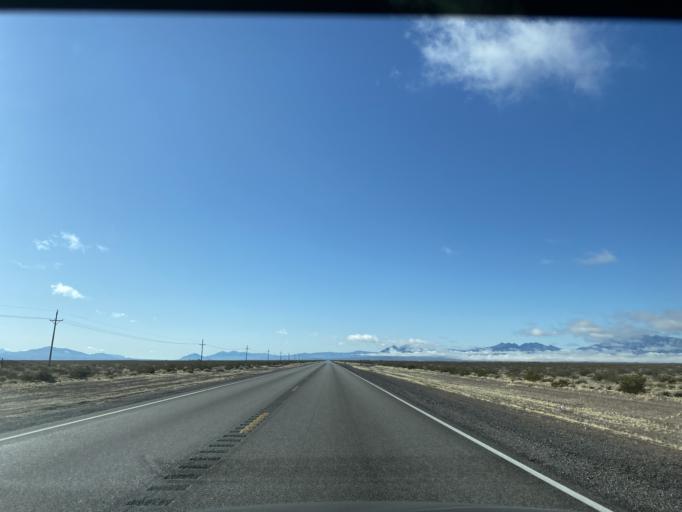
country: US
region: Nevada
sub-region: Nye County
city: Beatty
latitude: 36.6080
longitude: -116.4067
